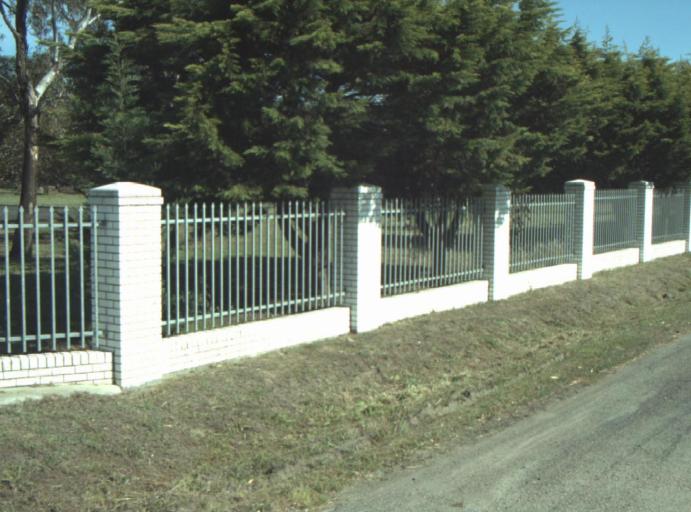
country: AU
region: Victoria
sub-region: Greater Geelong
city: Bell Post Hill
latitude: -38.0962
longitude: 144.3052
